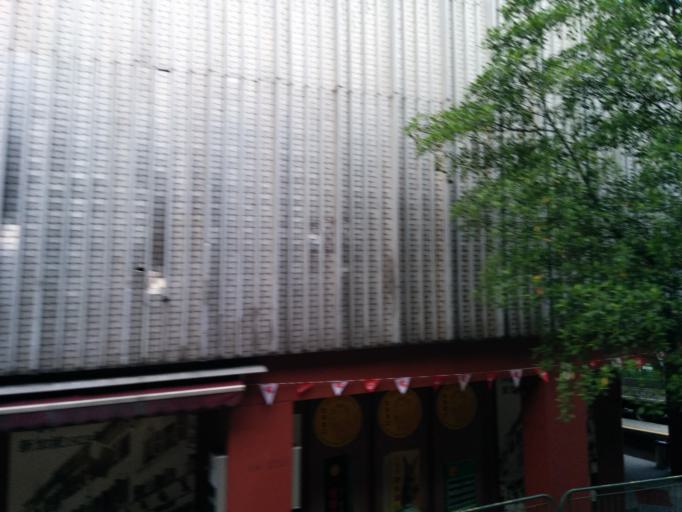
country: SG
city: Singapore
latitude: 1.2690
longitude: 103.8146
